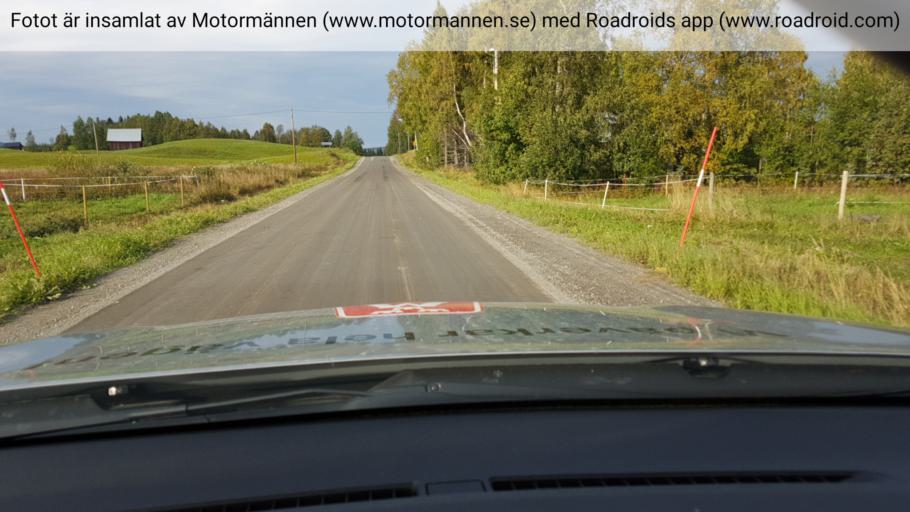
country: SE
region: Jaemtland
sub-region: Stroemsunds Kommun
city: Stroemsund
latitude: 64.0483
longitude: 15.8108
